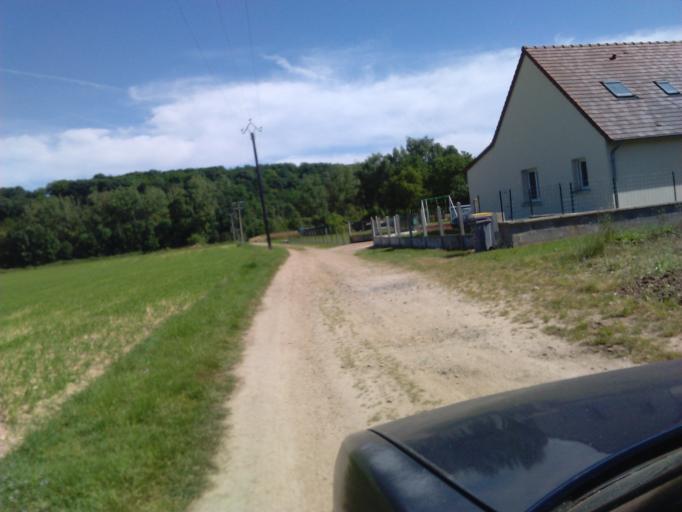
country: FR
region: Centre
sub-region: Departement du Loir-et-Cher
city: Villiers-sur-Loir
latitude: 47.8257
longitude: 0.9727
